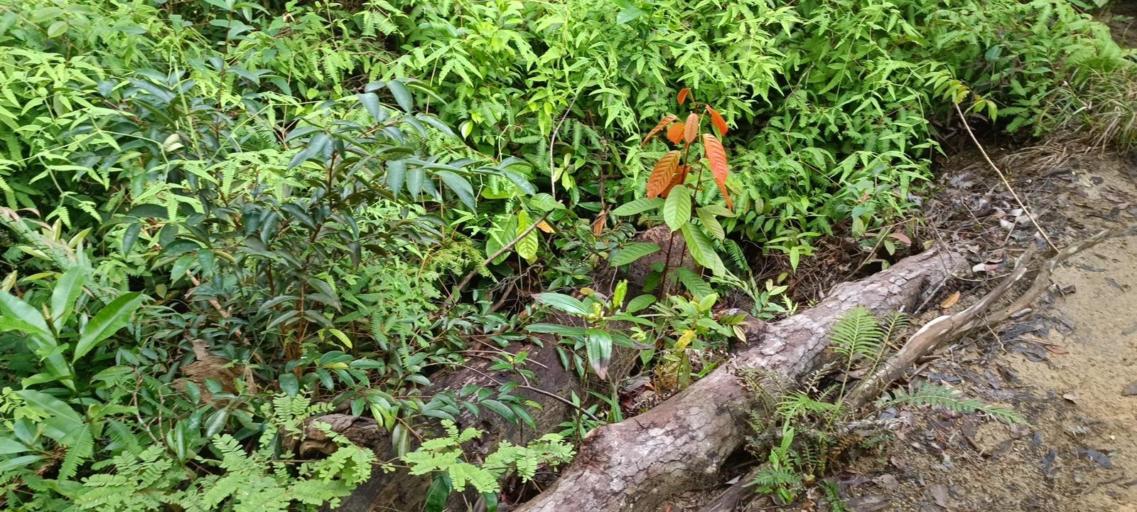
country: MY
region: Penang
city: Tanjung Tokong
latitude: 5.4269
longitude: 100.2880
